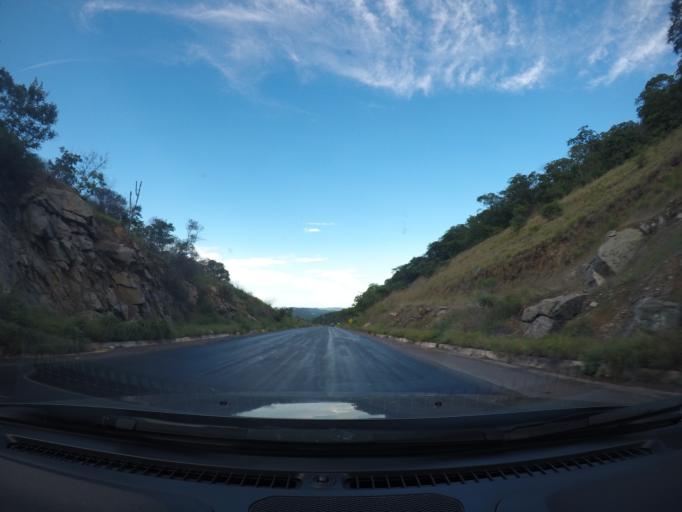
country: BR
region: Bahia
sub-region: Ibotirama
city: Ibotirama
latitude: -12.1416
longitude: -43.3532
